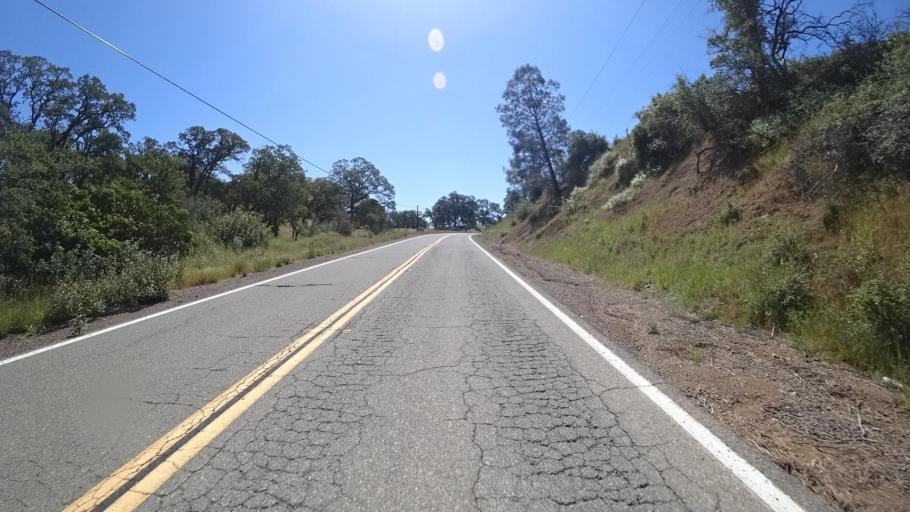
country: US
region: California
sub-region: Lake County
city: Hidden Valley Lake
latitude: 38.8832
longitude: -122.4519
